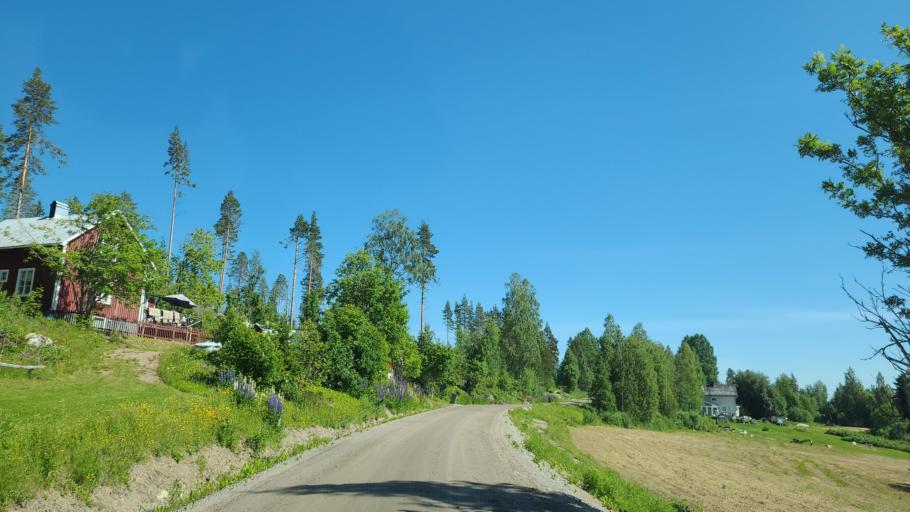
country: SE
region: Vaesterbotten
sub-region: Bjurholms Kommun
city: Bjurholm
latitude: 63.6753
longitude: 19.0227
